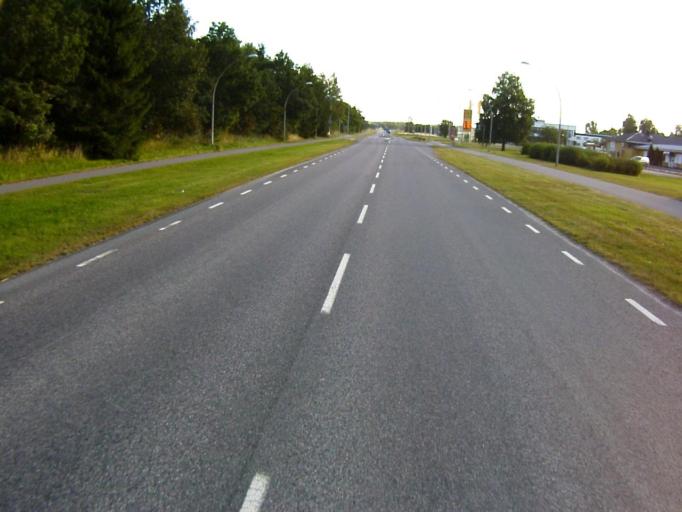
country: SE
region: Soedermanland
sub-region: Eskilstuna Kommun
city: Eskilstuna
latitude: 59.3683
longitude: 16.5465
